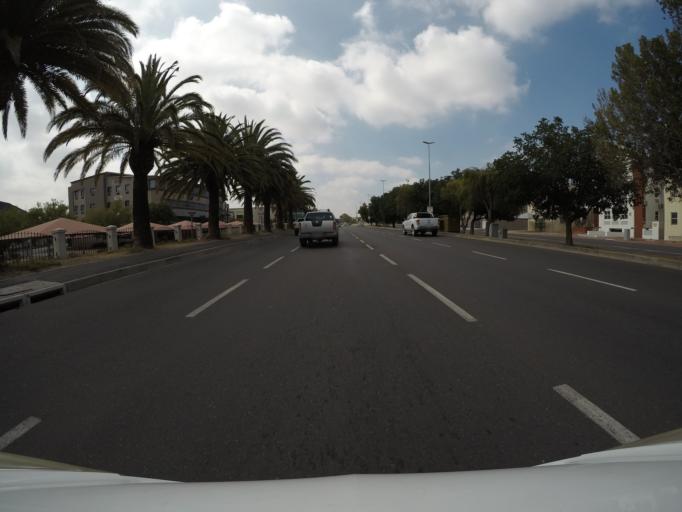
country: ZA
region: Western Cape
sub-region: City of Cape Town
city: Kraaifontein
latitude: -33.8793
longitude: 18.6357
